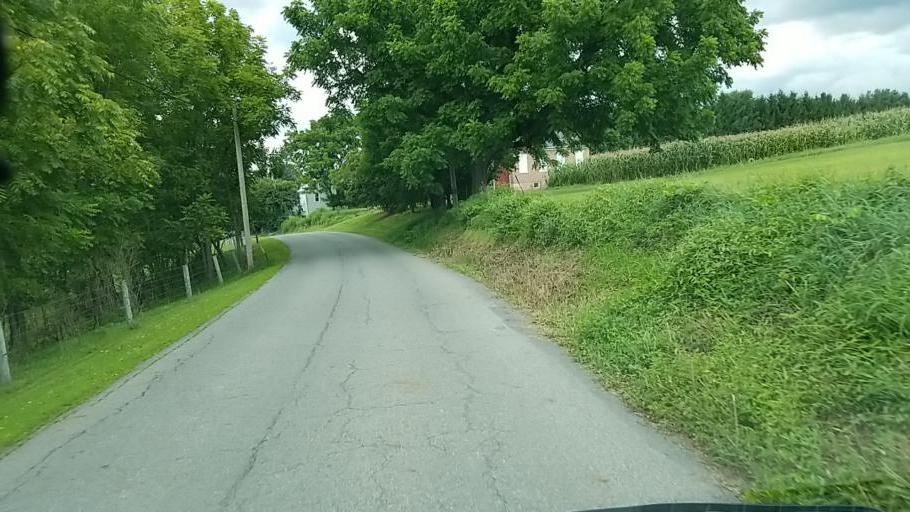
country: US
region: Pennsylvania
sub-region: Dauphin County
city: Elizabethville
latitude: 40.5943
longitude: -76.8020
